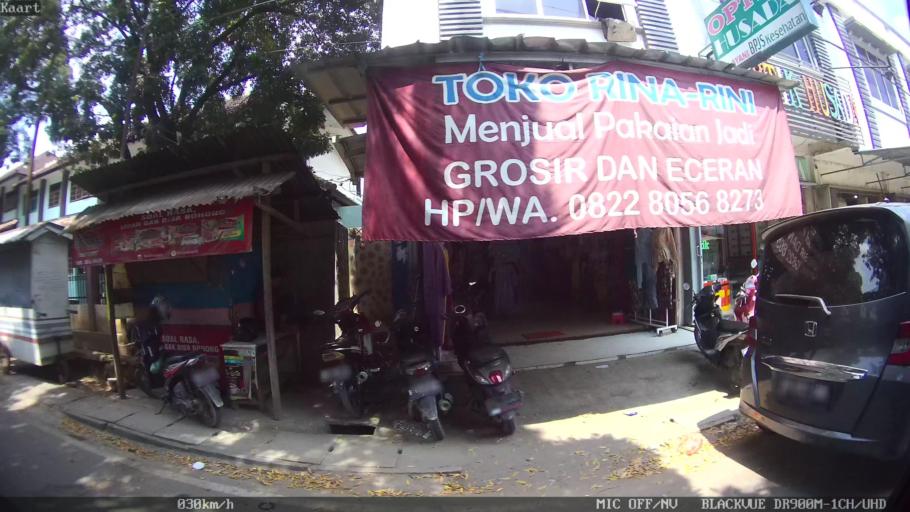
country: ID
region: Lampung
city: Pringsewu
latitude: -5.3573
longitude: 104.9770
